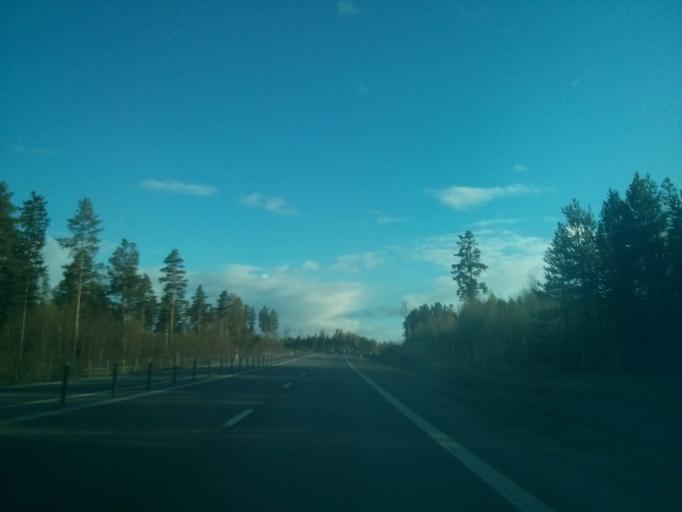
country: SE
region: Vaesternorrland
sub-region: Sundsvalls Kommun
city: Njurundabommen
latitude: 62.1315
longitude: 17.3369
